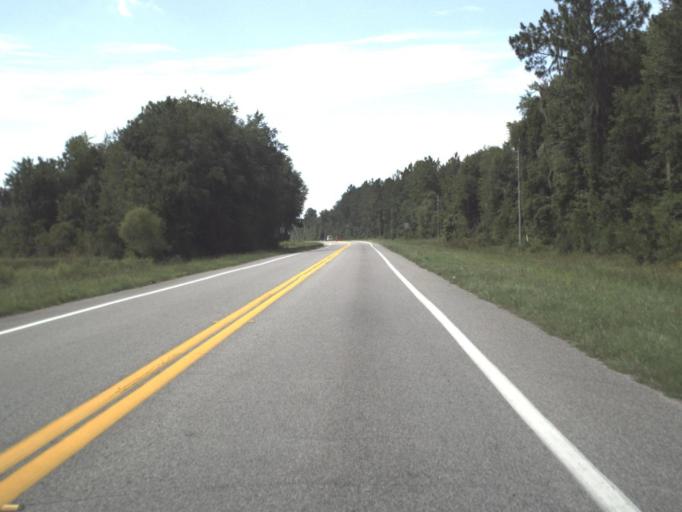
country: US
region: Florida
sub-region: Hamilton County
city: Jasper
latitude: 30.4433
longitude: -82.9337
